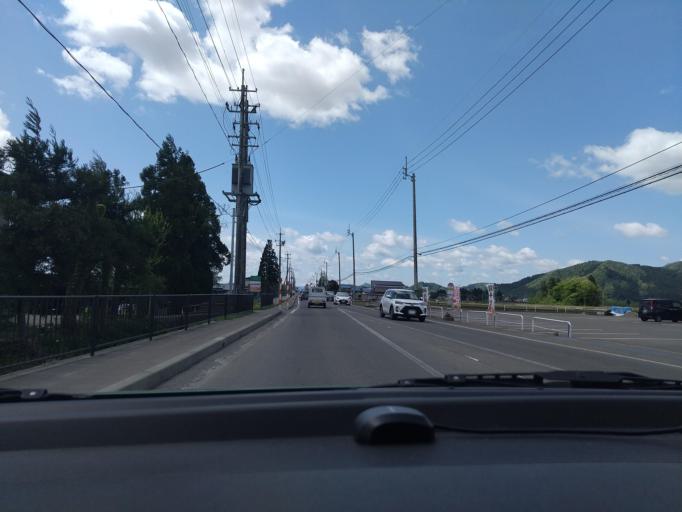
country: JP
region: Akita
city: Kakunodatemachi
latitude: 39.5571
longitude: 140.5545
